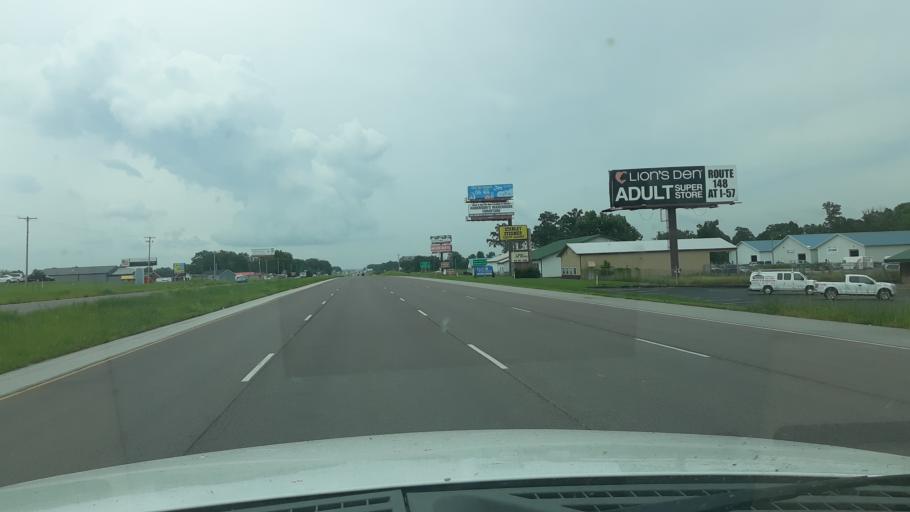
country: US
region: Illinois
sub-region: Williamson County
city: Crainville
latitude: 37.7449
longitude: -89.0499
